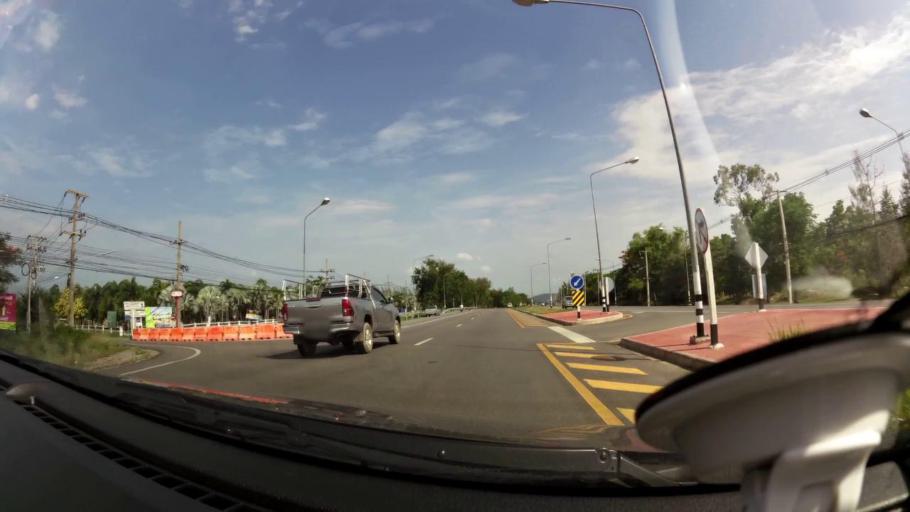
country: TH
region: Prachuap Khiri Khan
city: Hua Hin
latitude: 12.5137
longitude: 99.9664
